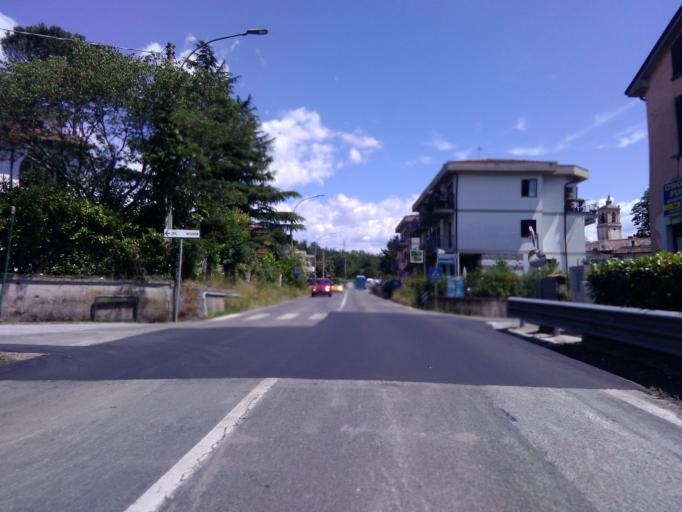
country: IT
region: Tuscany
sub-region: Provincia di Massa-Carrara
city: Terrarossa
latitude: 44.2310
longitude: 9.9622
